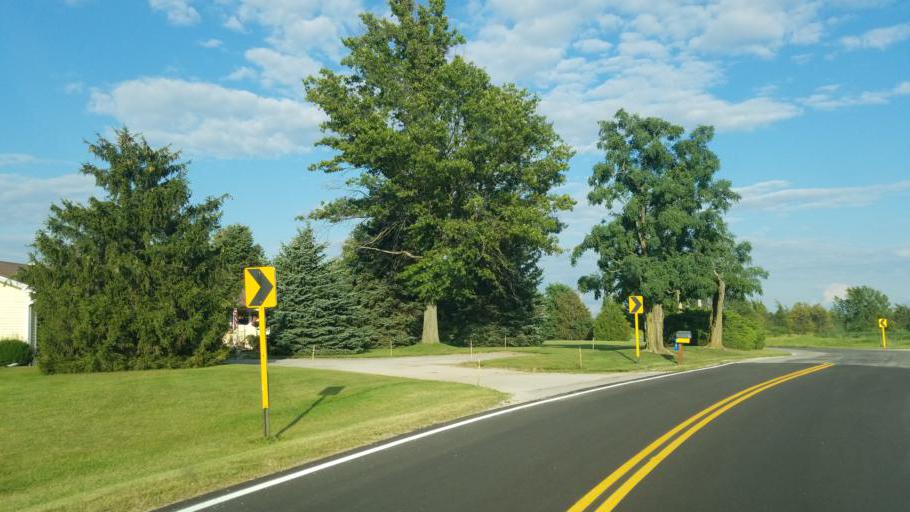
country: US
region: Ohio
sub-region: Seneca County
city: Tiffin
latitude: 41.1098
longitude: -83.0741
